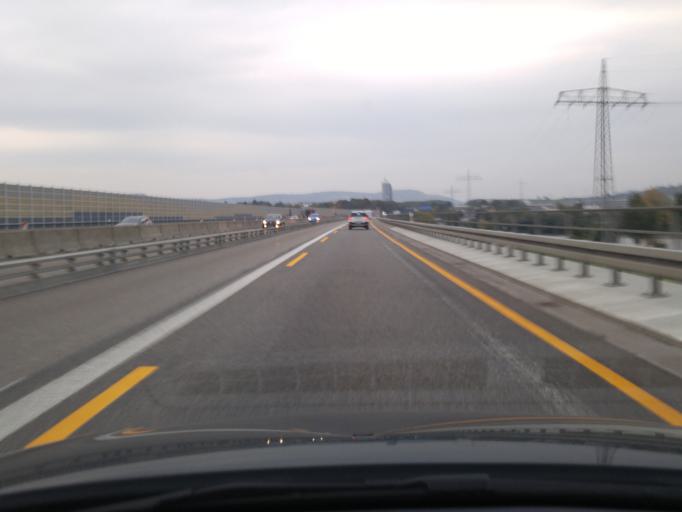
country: DE
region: Baden-Wuerttemberg
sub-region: Regierungsbezirk Stuttgart
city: Neckarsulm
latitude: 49.1849
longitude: 9.2101
